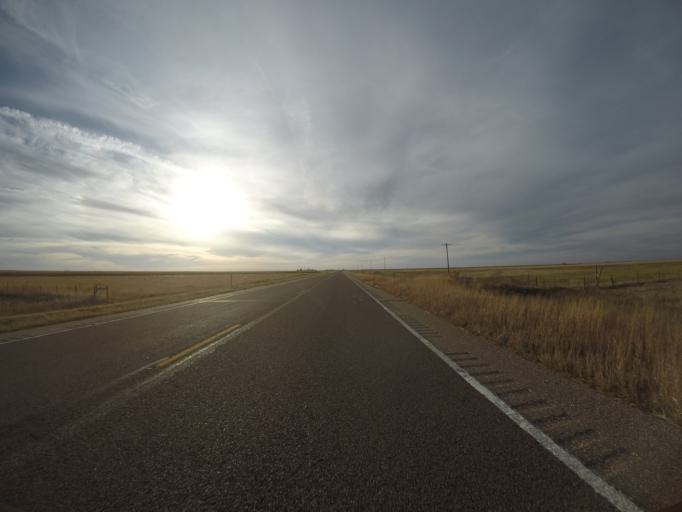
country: US
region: Colorado
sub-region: Kit Carson County
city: Burlington
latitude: 39.6583
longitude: -102.5457
